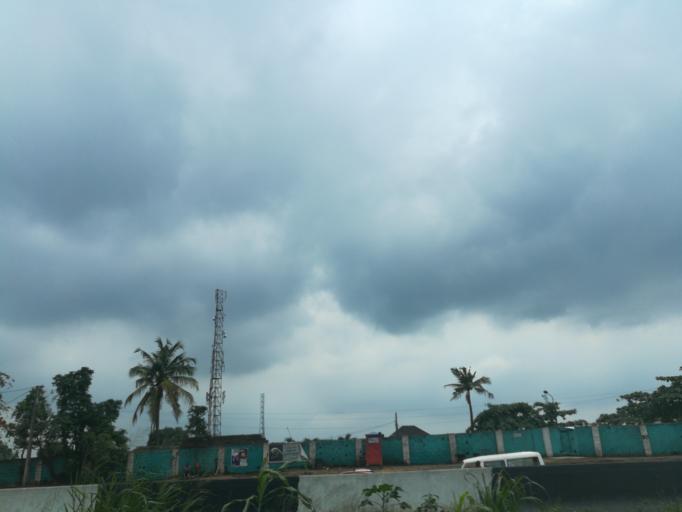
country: NG
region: Lagos
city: Ojota
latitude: 6.6063
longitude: 3.3730
